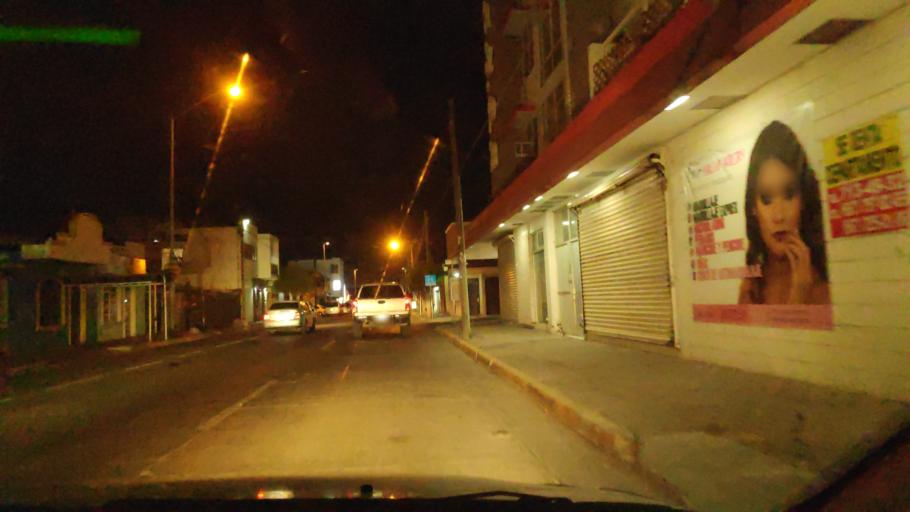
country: MX
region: Sinaloa
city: Culiacan
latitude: 24.8246
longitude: -107.3918
